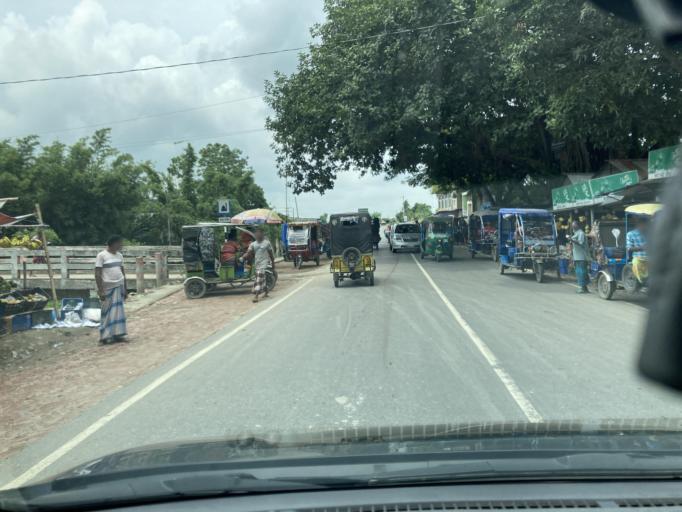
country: BD
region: Dhaka
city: Azimpur
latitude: 23.8062
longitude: 90.2016
